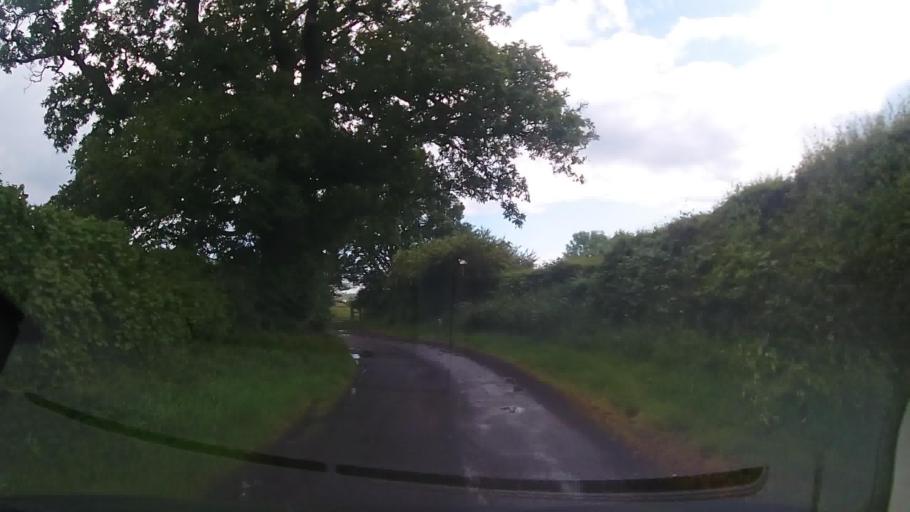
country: GB
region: England
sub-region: Telford and Wrekin
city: Ironbridge
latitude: 52.6470
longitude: -2.5082
